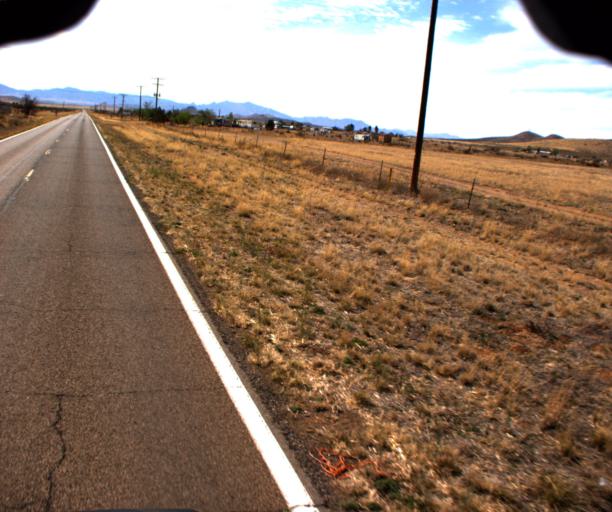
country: US
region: Arizona
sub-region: Cochise County
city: Willcox
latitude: 31.8837
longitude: -109.6767
